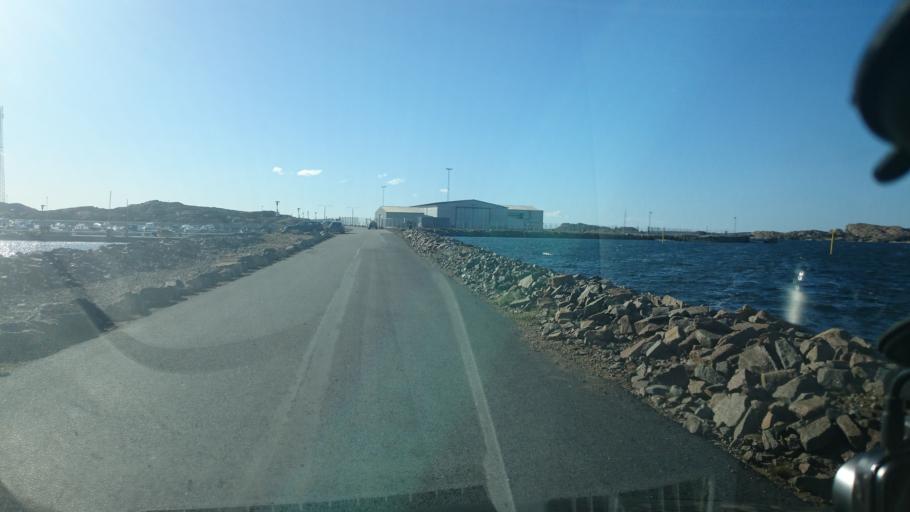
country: SE
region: Vaestra Goetaland
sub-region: Lysekils Kommun
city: Lysekil
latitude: 58.3175
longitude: 11.3996
